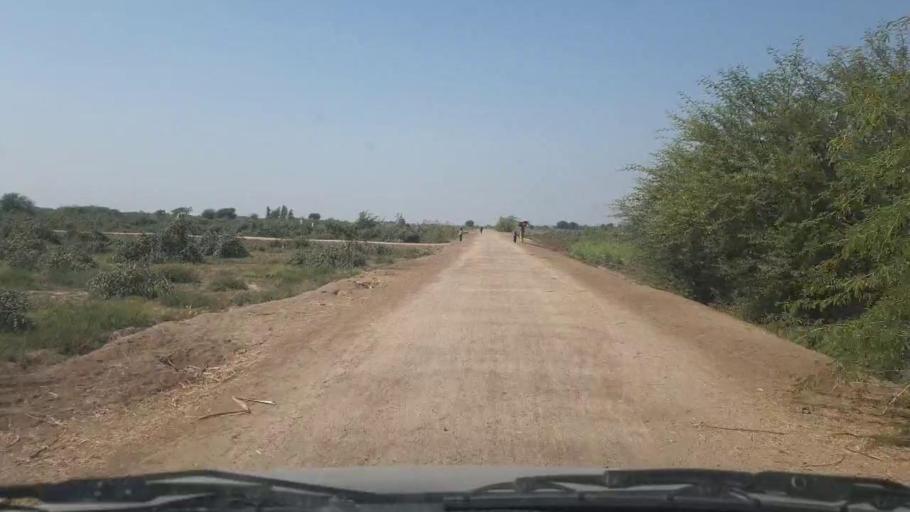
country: PK
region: Sindh
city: Samaro
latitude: 25.2385
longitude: 69.3370
